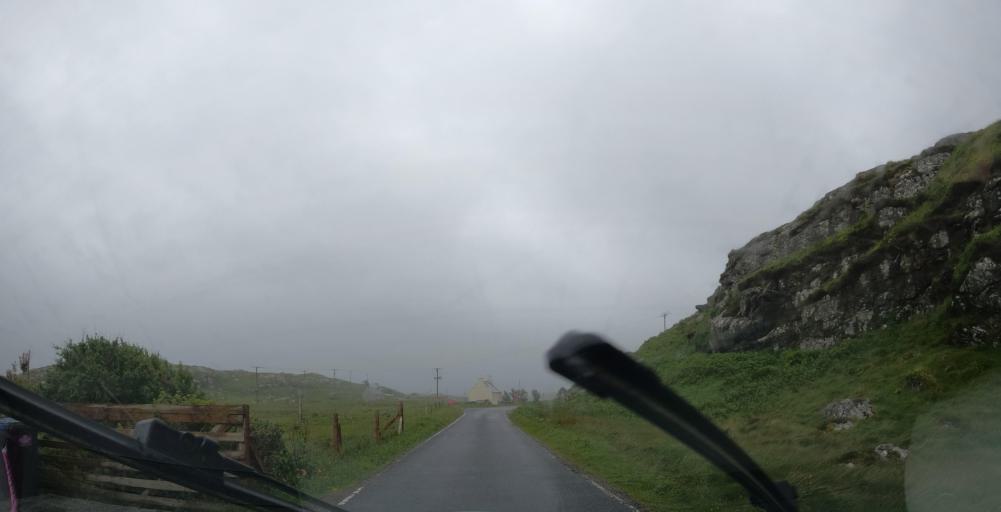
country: GB
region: Scotland
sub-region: Eilean Siar
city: Barra
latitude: 57.0140
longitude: -7.4311
